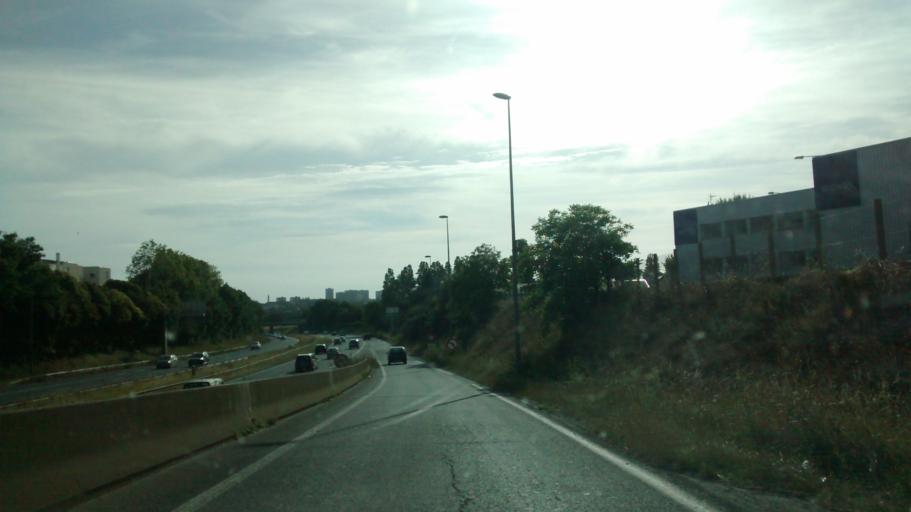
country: FR
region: Lower Normandy
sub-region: Departement du Calvados
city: Caen
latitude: 49.2027
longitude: -0.3635
